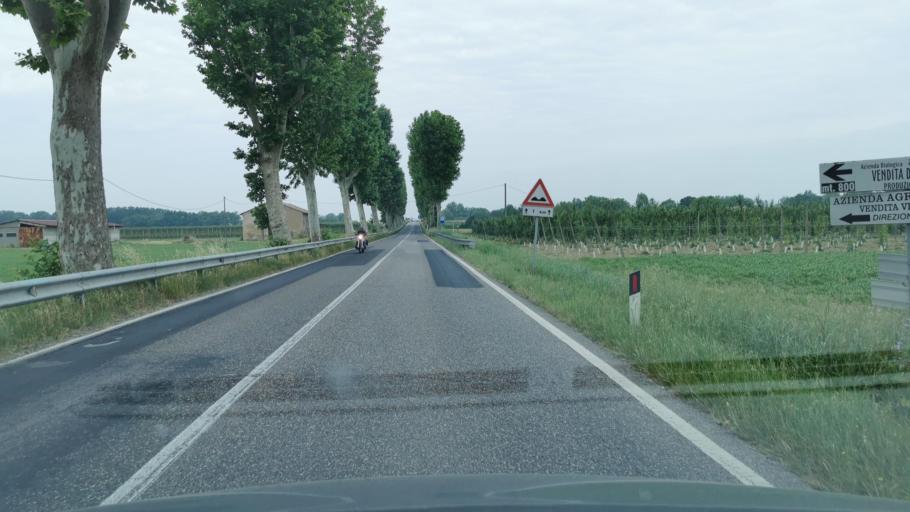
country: IT
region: Emilia-Romagna
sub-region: Provincia di Ravenna
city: Russi
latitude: 44.3991
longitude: 12.0297
